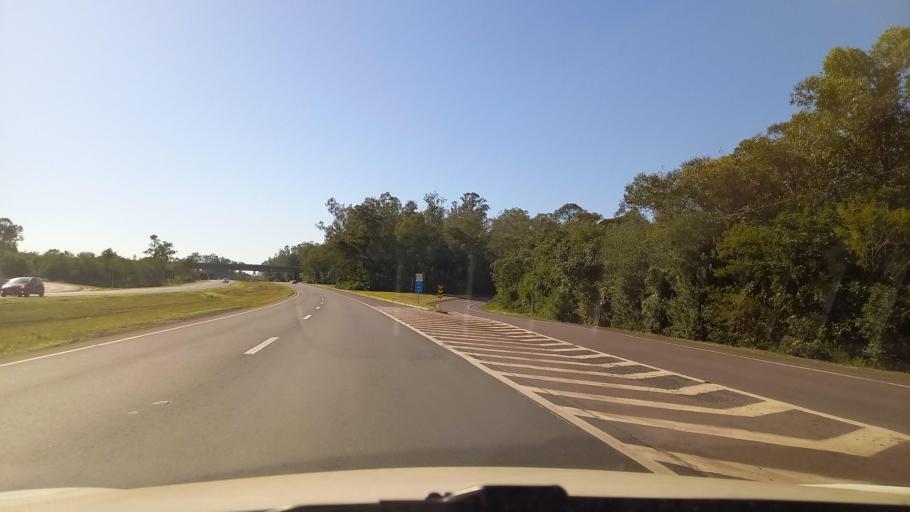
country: BR
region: Rio Grande do Sul
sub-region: Montenegro
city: Montenegro
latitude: -29.8180
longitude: -51.4222
